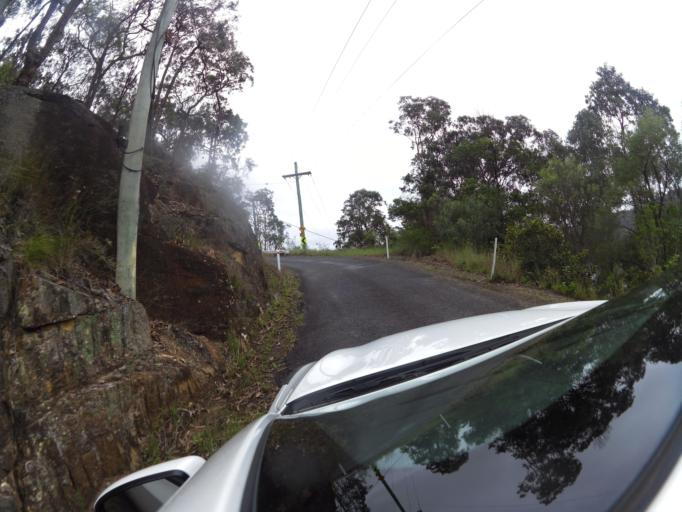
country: AU
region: New South Wales
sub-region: Hornsby Shire
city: Glenorie
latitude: -33.4273
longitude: 150.9540
